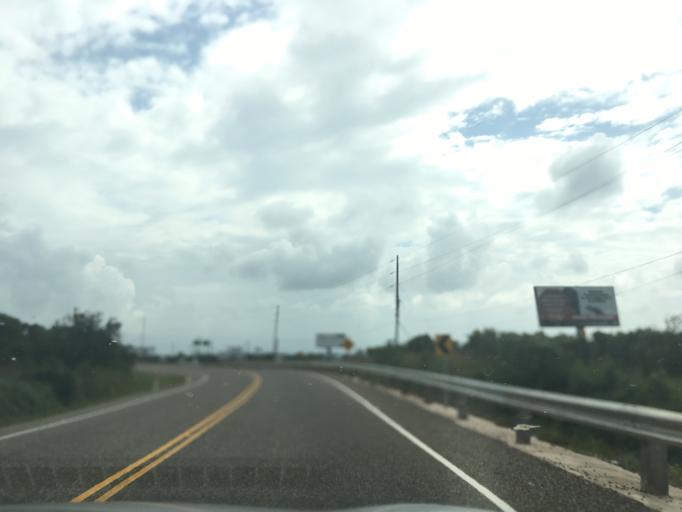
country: BZ
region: Stann Creek
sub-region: Dangriga
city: Dangriga
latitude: 16.9822
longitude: -88.2959
